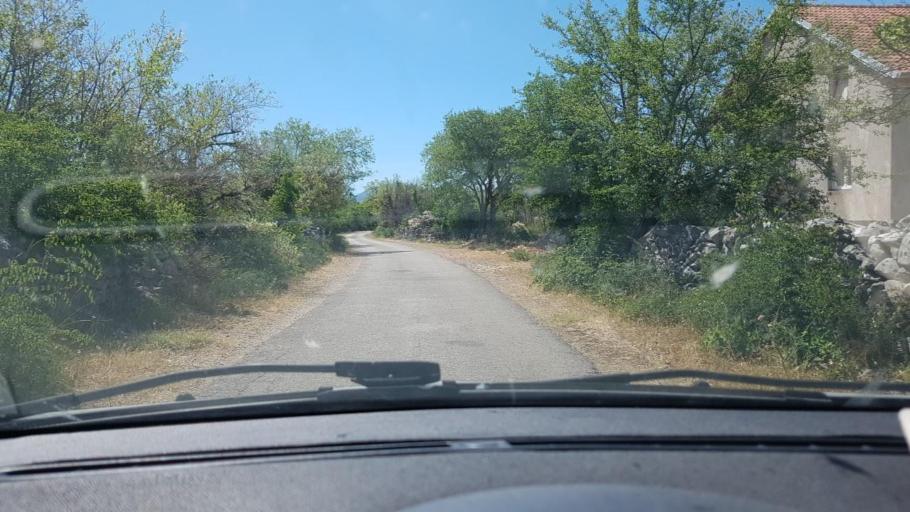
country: HR
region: Sibensko-Kniniska
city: Kistanje
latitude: 44.0377
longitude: 16.0576
